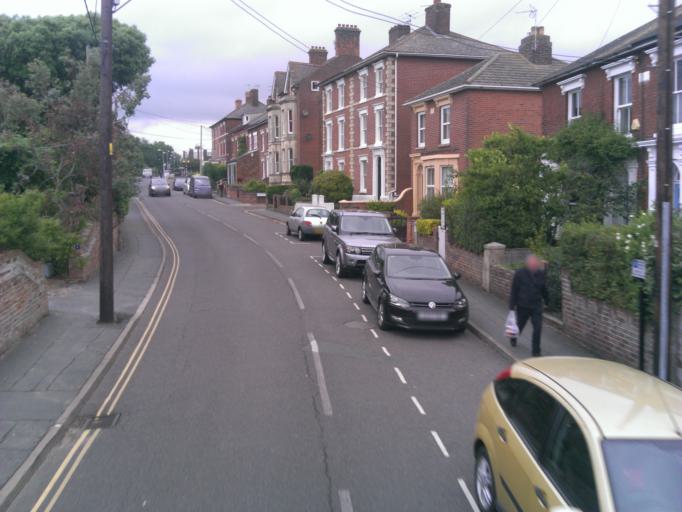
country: GB
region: England
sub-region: Essex
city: Wivenhoe
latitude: 51.8581
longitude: 0.9599
